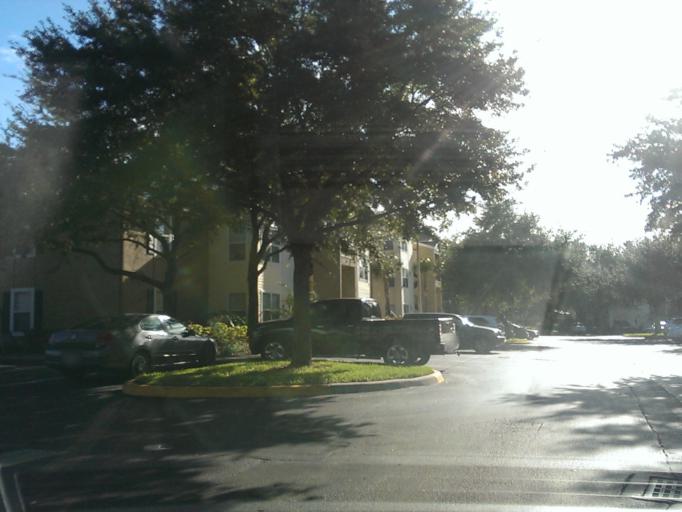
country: US
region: Florida
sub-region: Lake County
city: Four Corners
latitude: 28.3645
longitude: -81.6762
